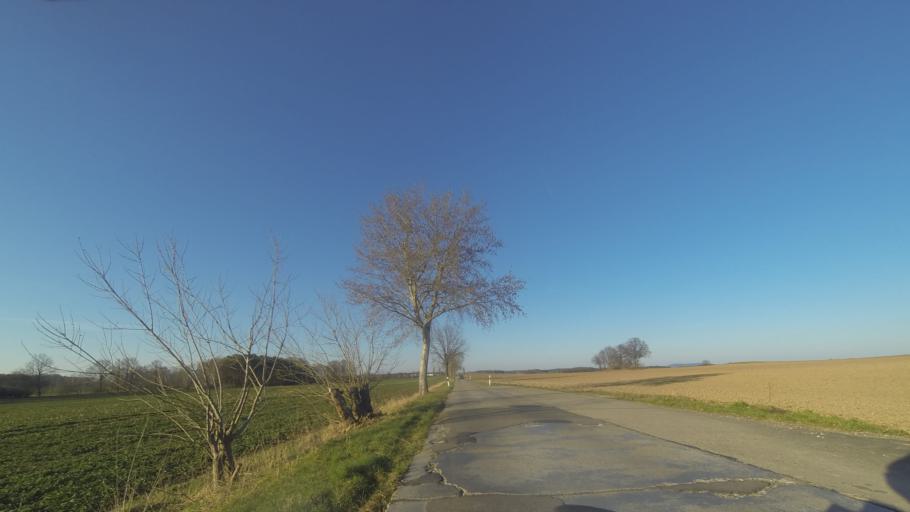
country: DE
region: Saxony
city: Radeburg
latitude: 51.1695
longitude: 13.7709
